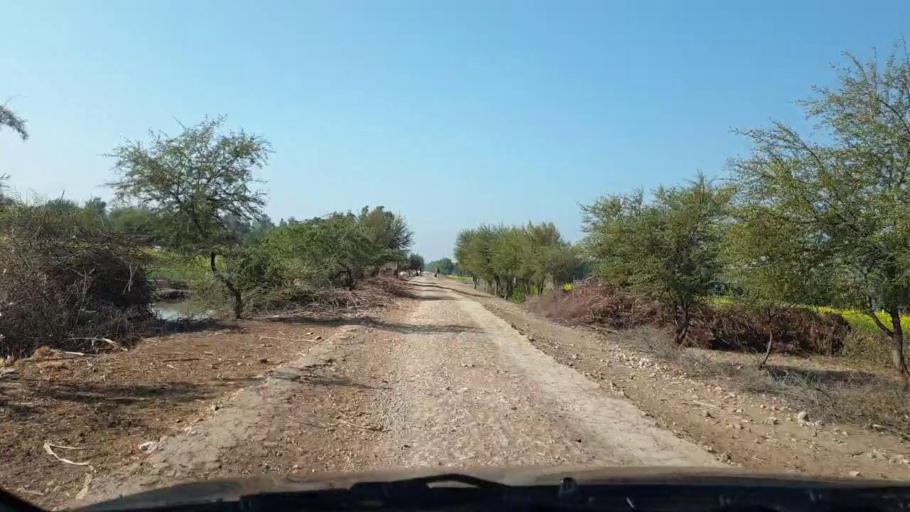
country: PK
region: Sindh
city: Sinjhoro
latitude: 26.0005
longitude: 68.7667
